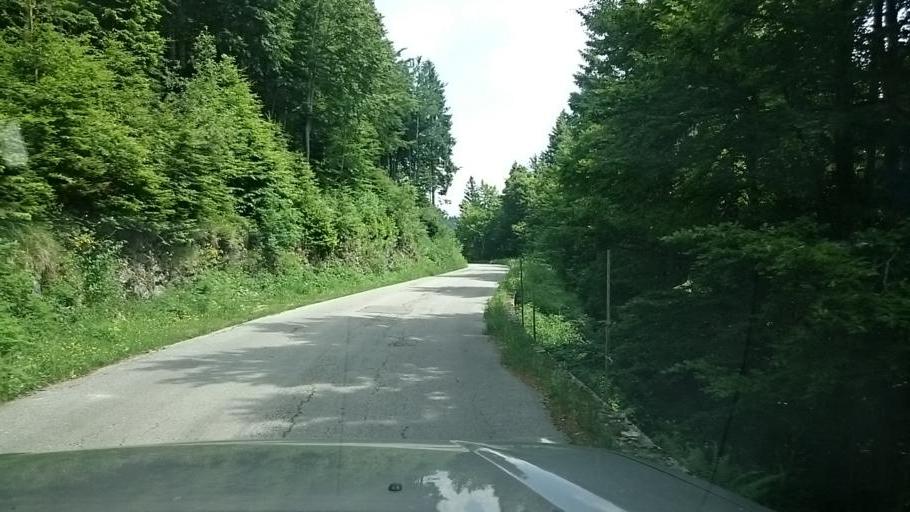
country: IT
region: Veneto
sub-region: Provincia di Vicenza
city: Foza
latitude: 45.9333
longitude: 11.6300
